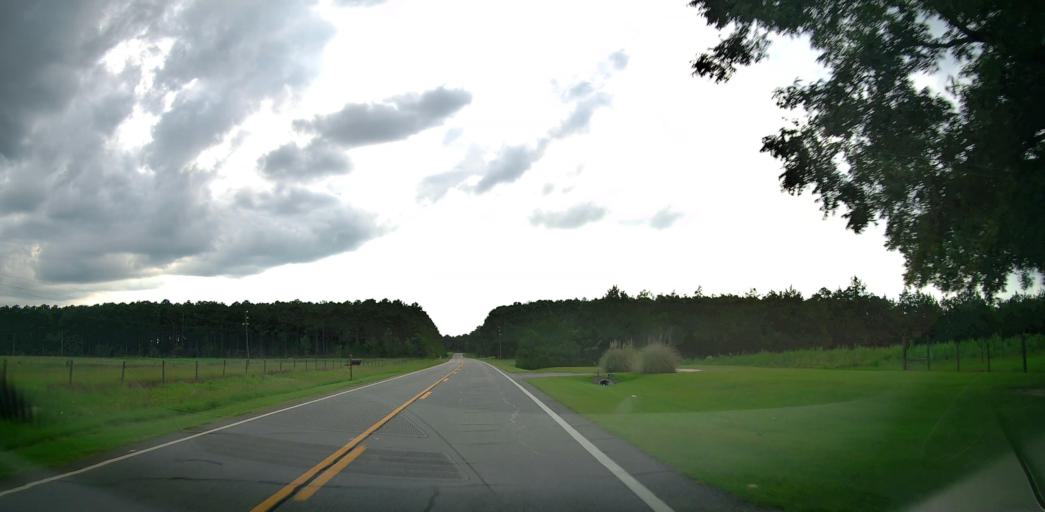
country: US
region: Georgia
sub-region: Pulaski County
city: Hawkinsville
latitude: 32.2918
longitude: -83.5089
